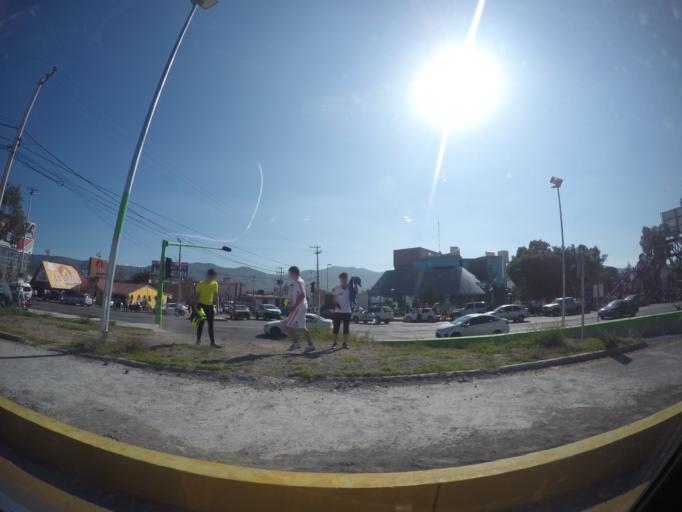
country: MX
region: Hidalgo
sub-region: Mineral de la Reforma
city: Campestre Villas del Alamo
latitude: 20.0968
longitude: -98.7156
